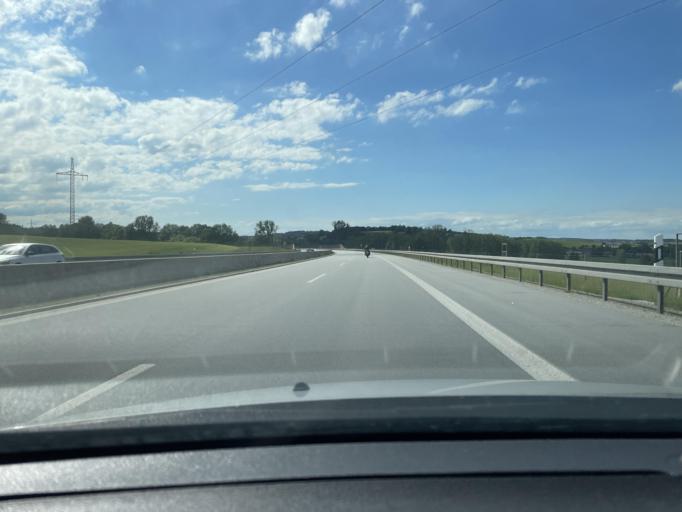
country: DE
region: Bavaria
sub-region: Upper Bavaria
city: Schwindegg
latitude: 48.2536
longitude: 12.2436
